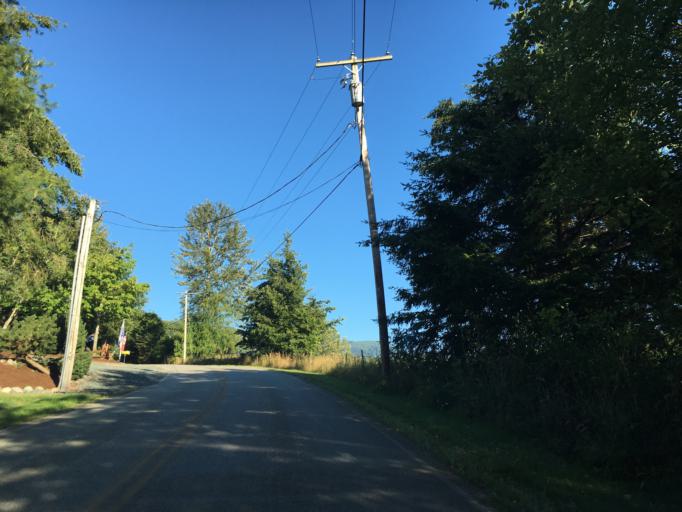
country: US
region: Washington
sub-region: Whatcom County
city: Nooksack
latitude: 48.9425
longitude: -122.3058
